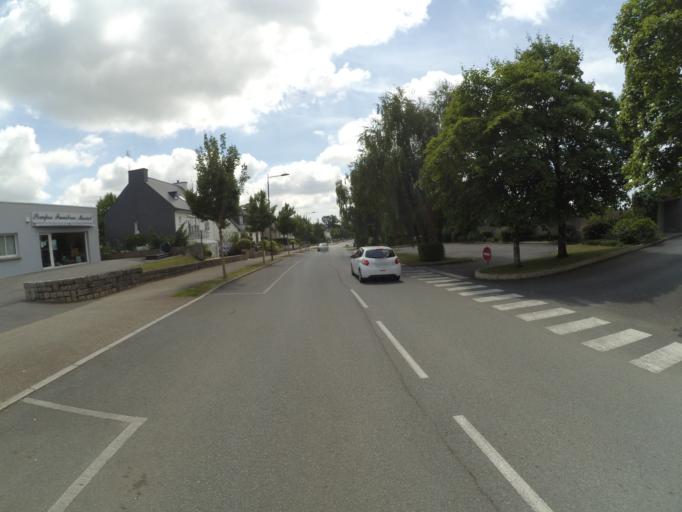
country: FR
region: Brittany
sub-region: Departement du Finistere
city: Rosporden
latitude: 47.9656
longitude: -3.8298
